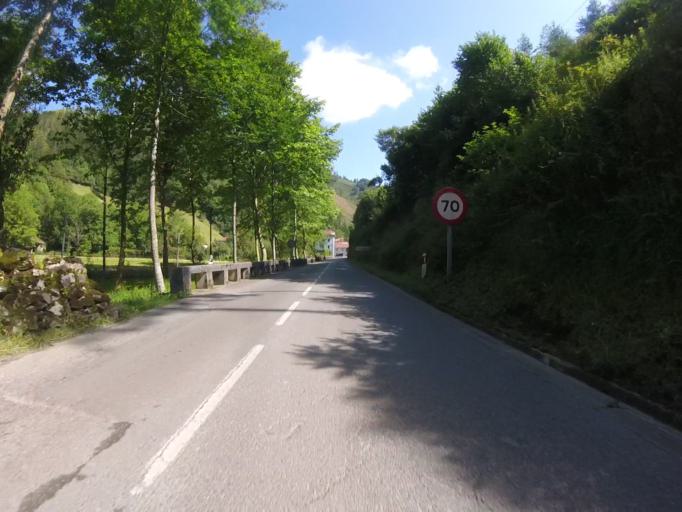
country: ES
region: Basque Country
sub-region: Provincia de Guipuzcoa
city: Beizama
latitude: 43.1063
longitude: -2.2419
